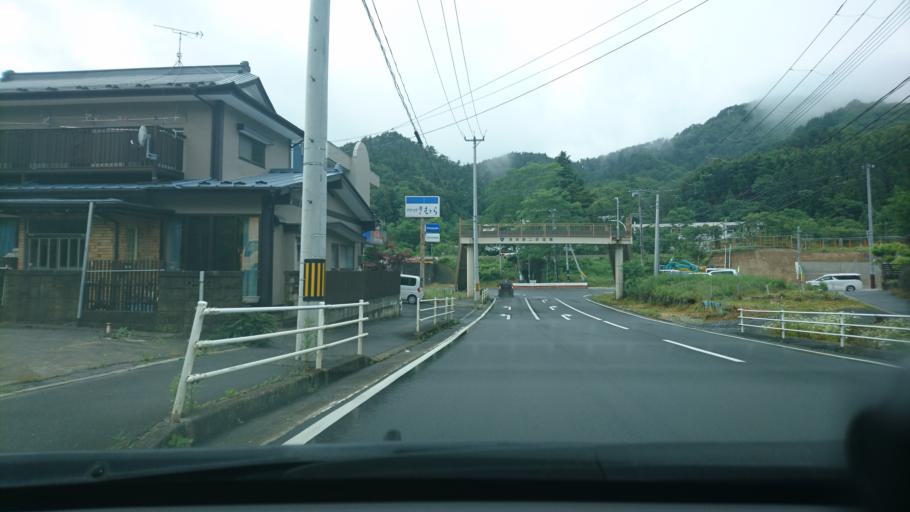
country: JP
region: Miyagi
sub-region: Oshika Gun
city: Onagawa Cho
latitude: 38.4383
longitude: 141.4311
